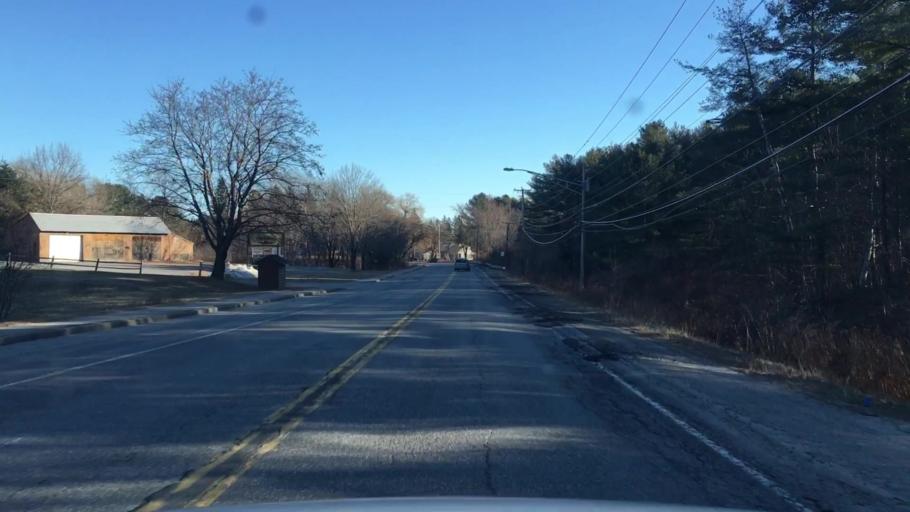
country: US
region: Maine
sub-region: Kennebec County
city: Waterville
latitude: 44.5305
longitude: -69.6609
